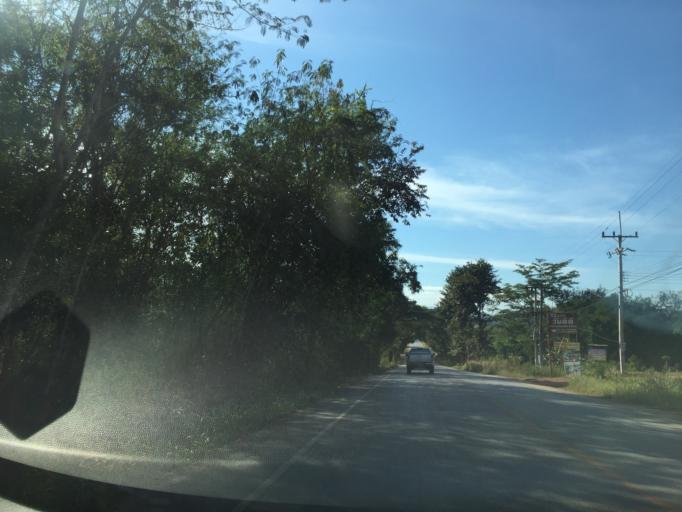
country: TH
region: Loei
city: Wang Saphung
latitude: 17.3153
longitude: 101.7416
